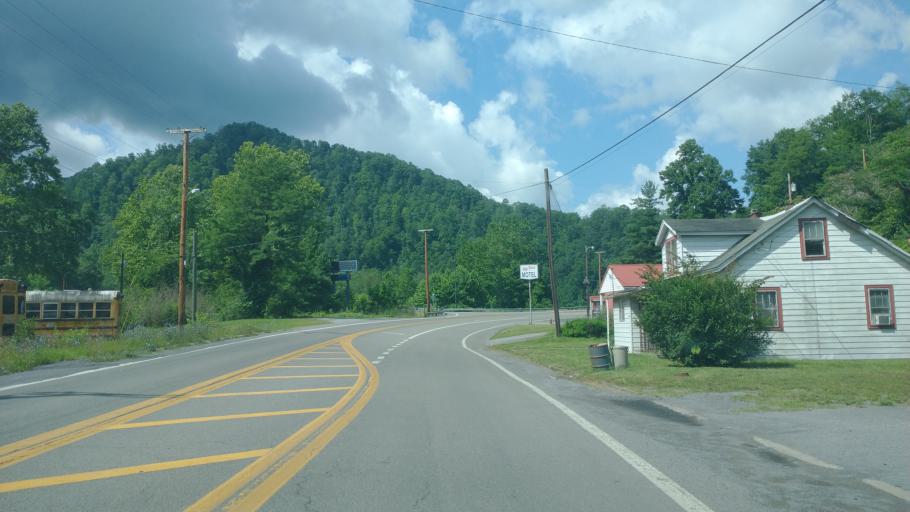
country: US
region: West Virginia
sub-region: McDowell County
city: Welch
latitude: 37.4148
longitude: -81.5212
